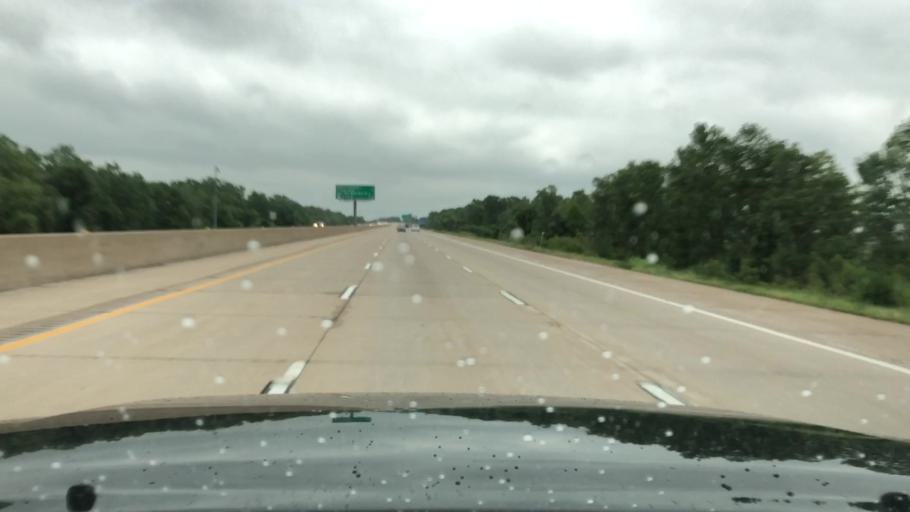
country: US
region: Missouri
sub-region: Saint Charles County
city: Saint Peters
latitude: 38.8152
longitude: -90.5752
